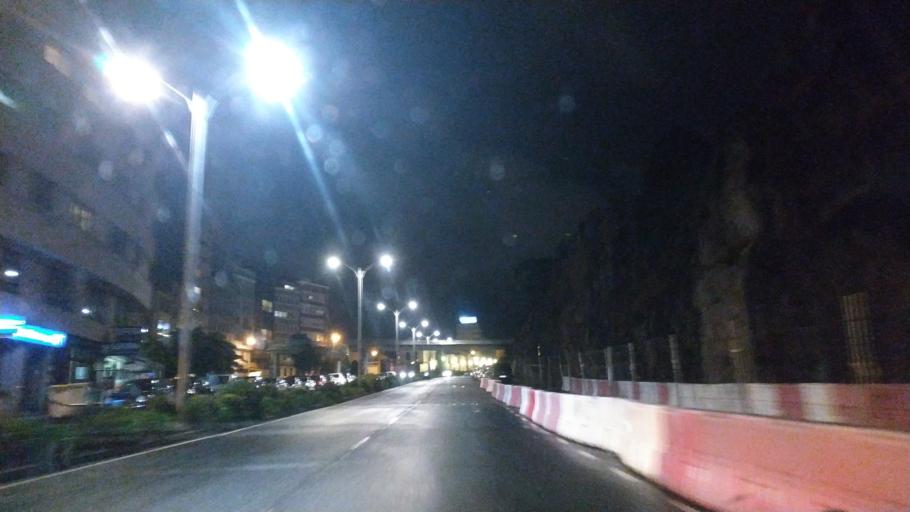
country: ES
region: Galicia
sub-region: Provincia da Coruna
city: A Coruna
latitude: 43.3621
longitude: -8.4106
